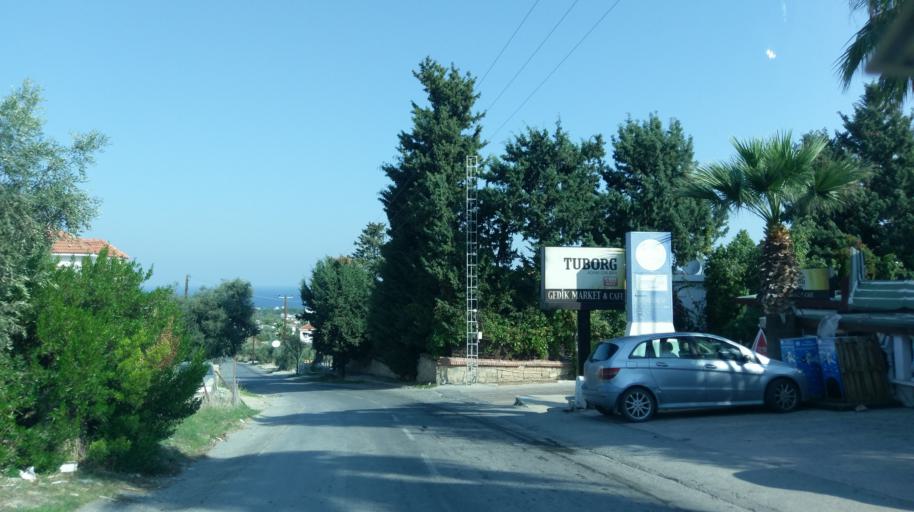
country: CY
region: Keryneia
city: Kyrenia
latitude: 35.3310
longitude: 33.2606
